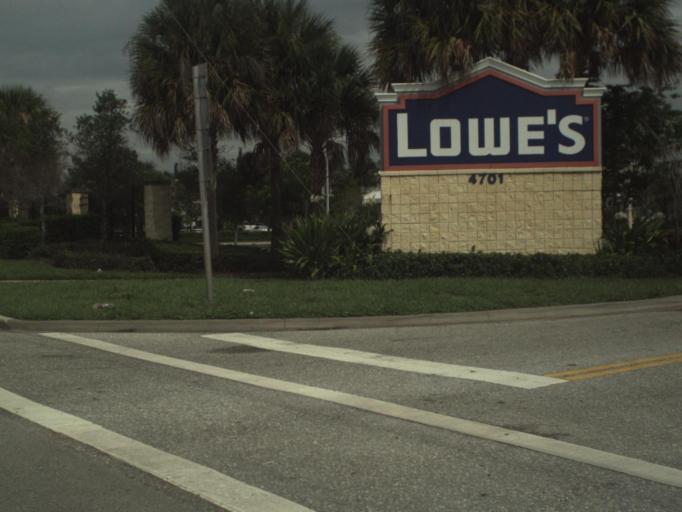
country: US
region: Florida
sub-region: Palm Beach County
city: Schall Circle
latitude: 26.7071
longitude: -80.1137
